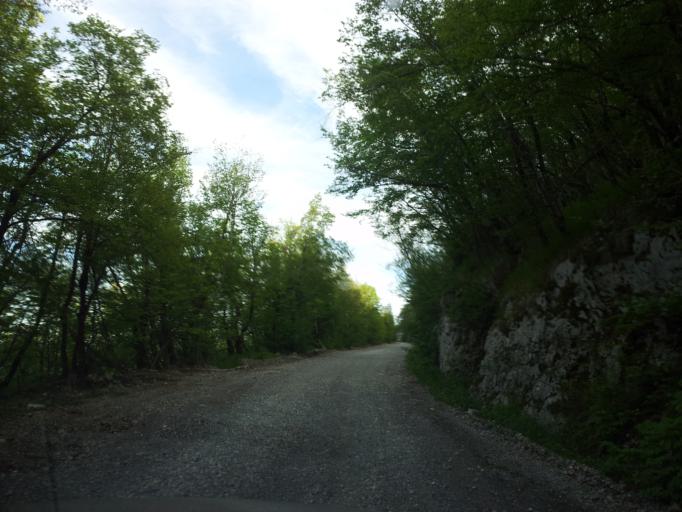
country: HR
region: Zadarska
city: Obrovac
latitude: 44.2993
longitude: 15.6644
